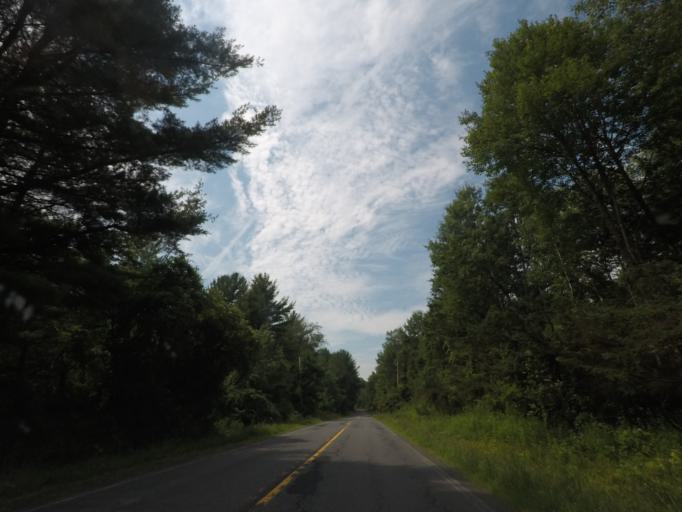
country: US
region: New York
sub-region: Rensselaer County
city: Wynantskill
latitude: 42.7448
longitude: -73.6053
